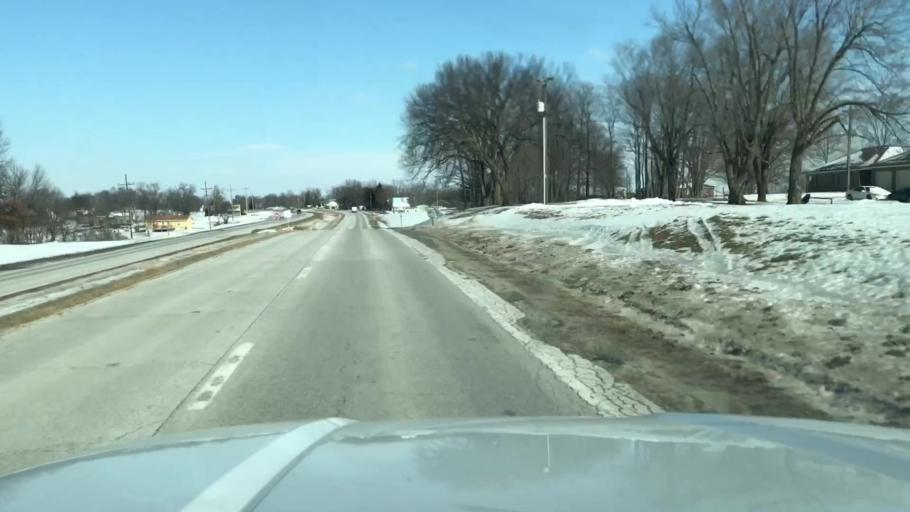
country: US
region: Missouri
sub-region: Andrew County
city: Savannah
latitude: 39.9042
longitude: -94.8098
